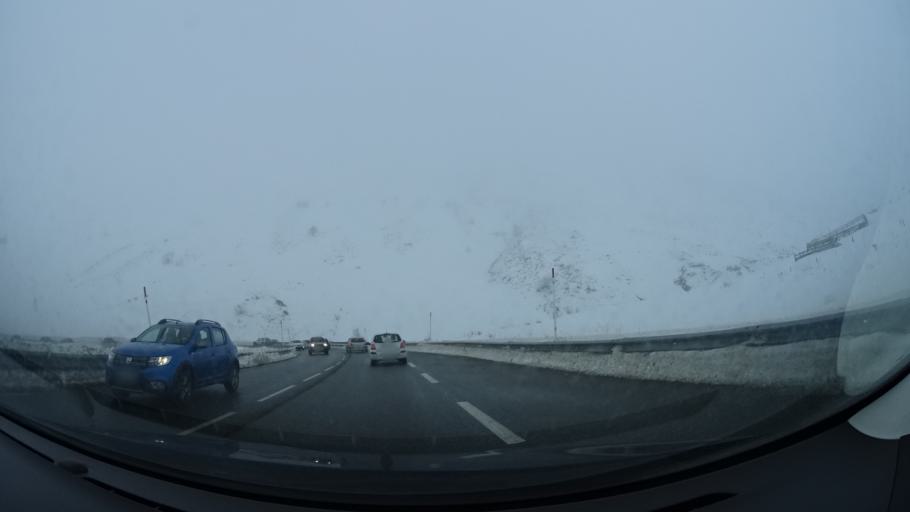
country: AD
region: Encamp
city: Pas de la Casa
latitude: 42.5572
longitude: 1.7677
